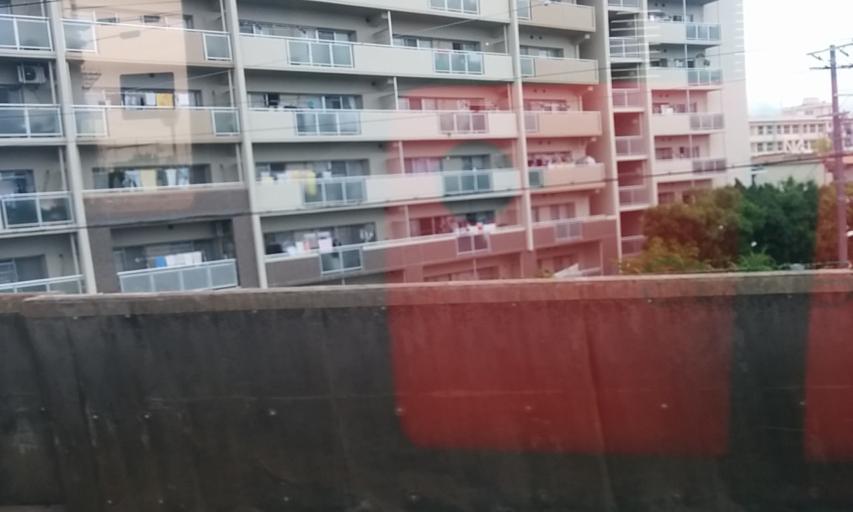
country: JP
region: Osaka
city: Toyonaka
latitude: 34.7666
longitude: 135.4728
